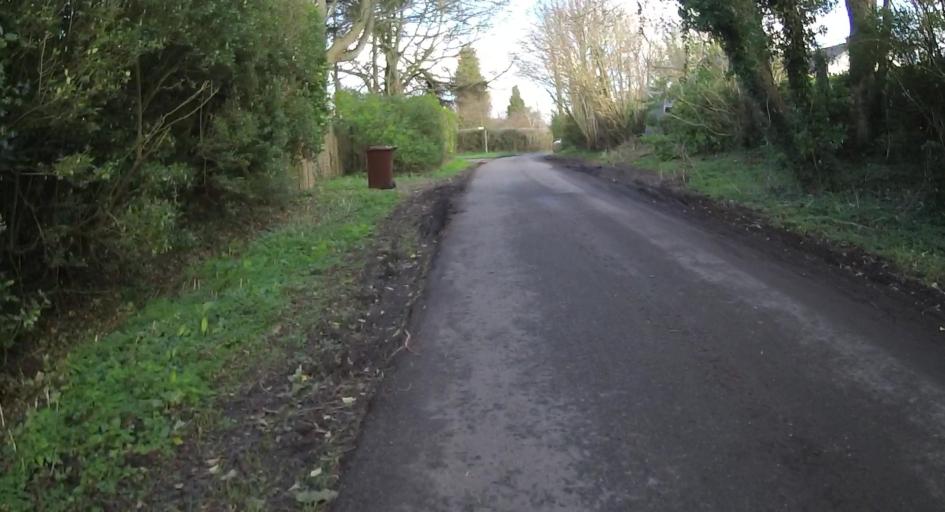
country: GB
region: England
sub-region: Hampshire
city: Four Marks
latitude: 51.1165
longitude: -1.0809
